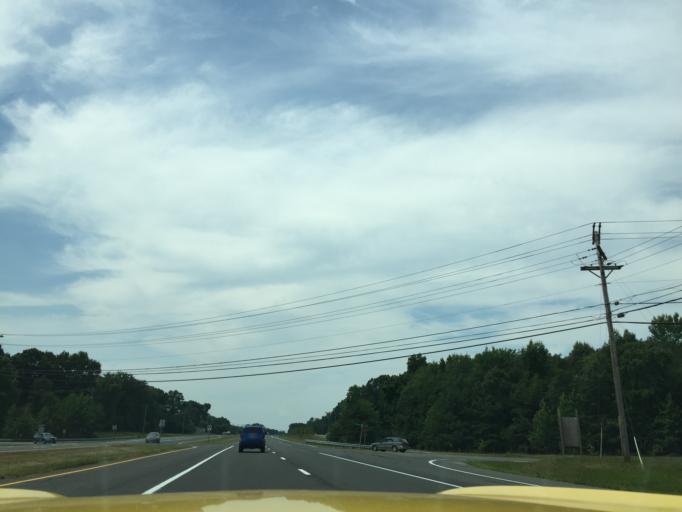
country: US
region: Maryland
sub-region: Charles County
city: Bryans Road
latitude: 38.6387
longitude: -77.0501
